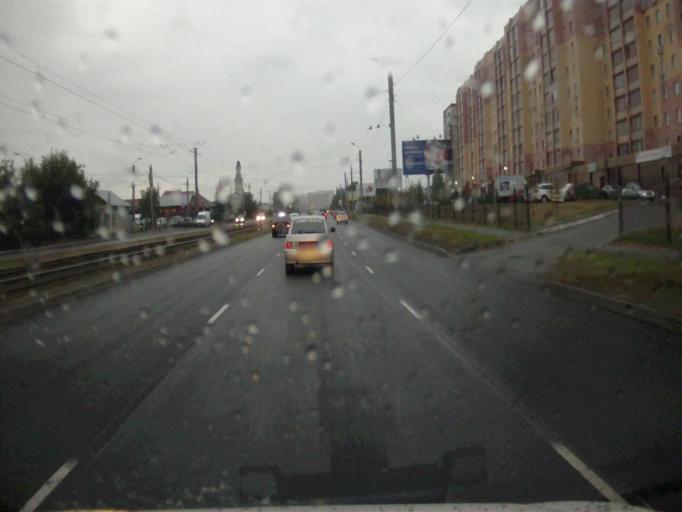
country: RU
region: Chelyabinsk
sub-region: Gorod Chelyabinsk
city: Chelyabinsk
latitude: 55.1839
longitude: 61.3712
